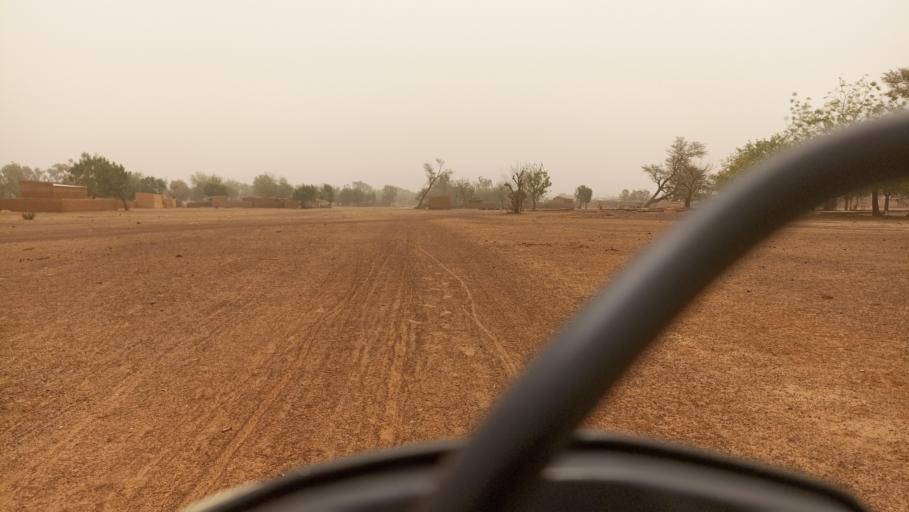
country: BF
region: Nord
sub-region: Province du Zondoma
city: Gourcy
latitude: 13.2485
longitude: -2.5923
